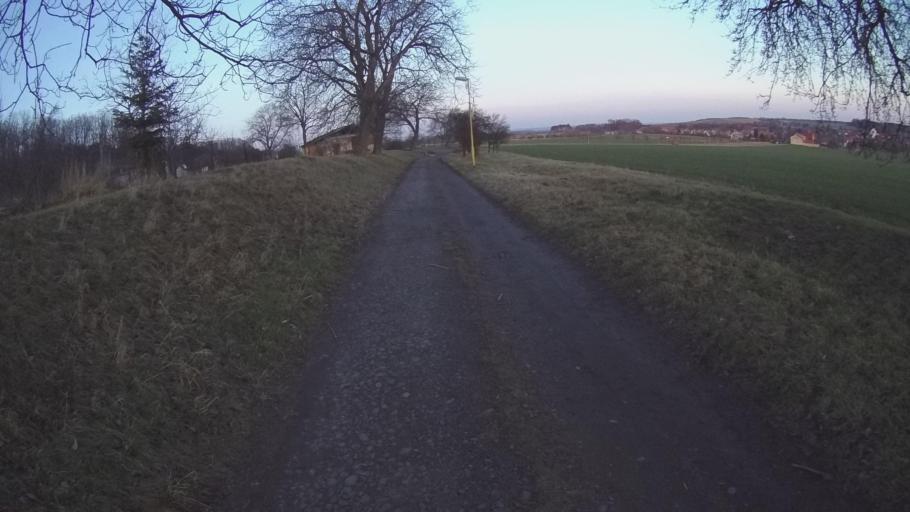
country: CZ
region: Ustecky
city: Bechlin
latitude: 50.3791
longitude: 14.2978
